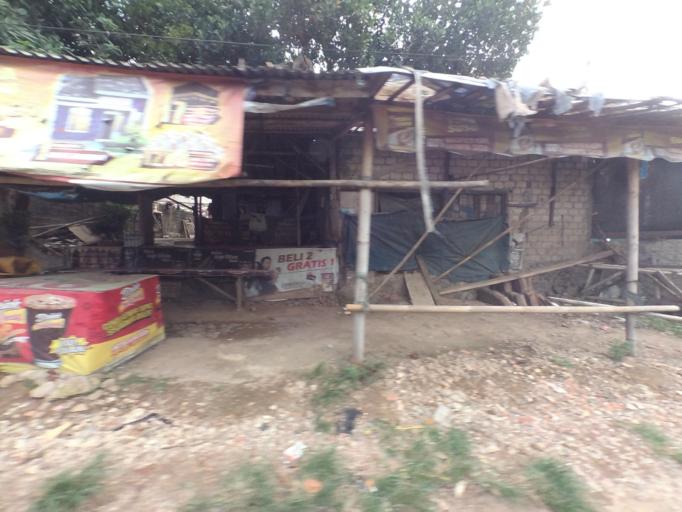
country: ID
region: West Java
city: Ciampea
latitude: -6.5596
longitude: 106.6890
